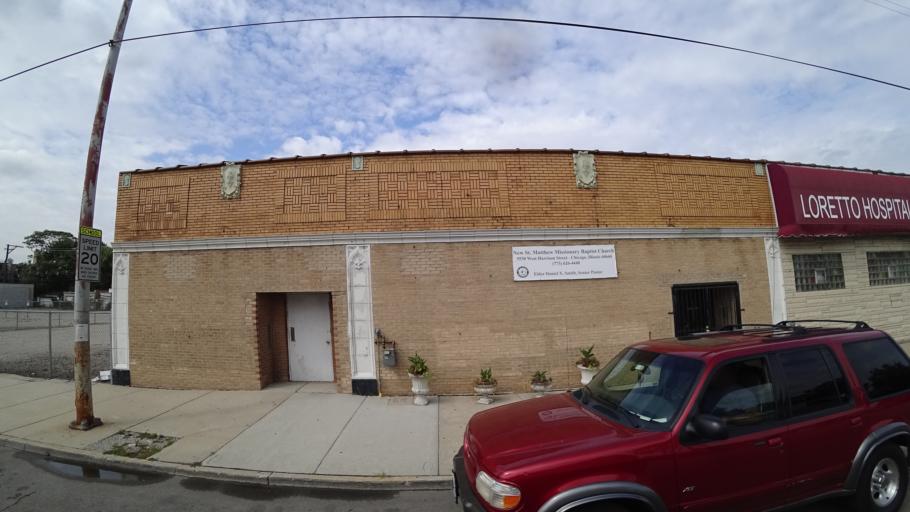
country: US
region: Illinois
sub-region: Cook County
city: Oak Park
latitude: 41.8729
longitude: -87.7627
